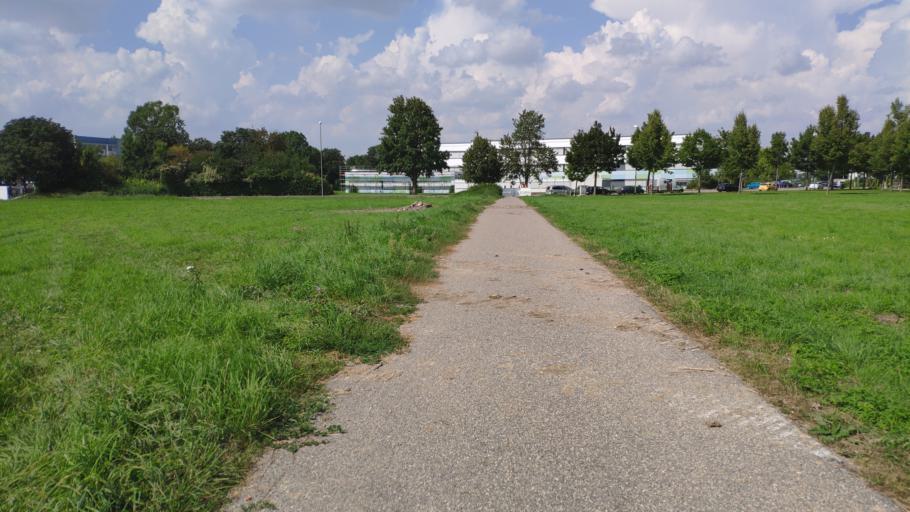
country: DE
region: Bavaria
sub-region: Swabia
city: Neu-Ulm
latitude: 48.3754
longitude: 10.0022
